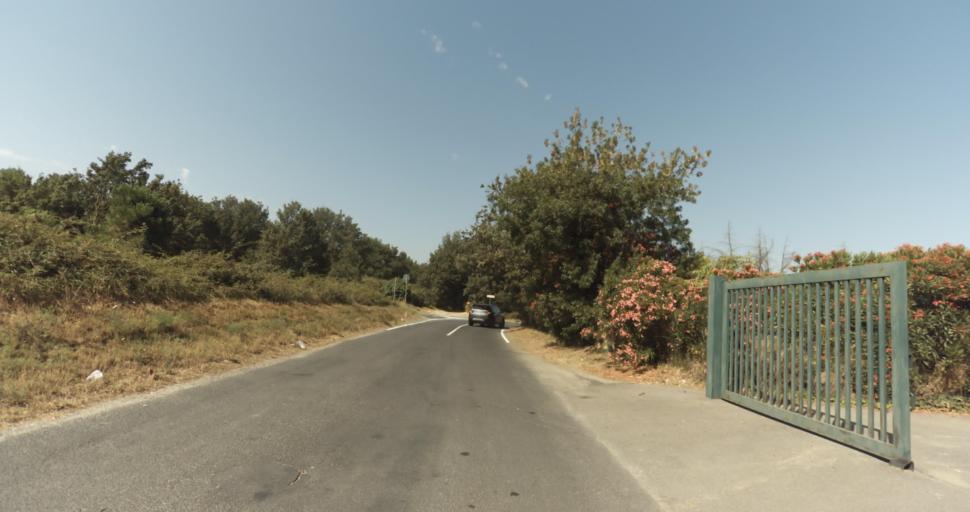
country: FR
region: Languedoc-Roussillon
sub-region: Departement des Pyrenees-Orientales
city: Latour-Bas-Elne
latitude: 42.6136
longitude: 2.9895
